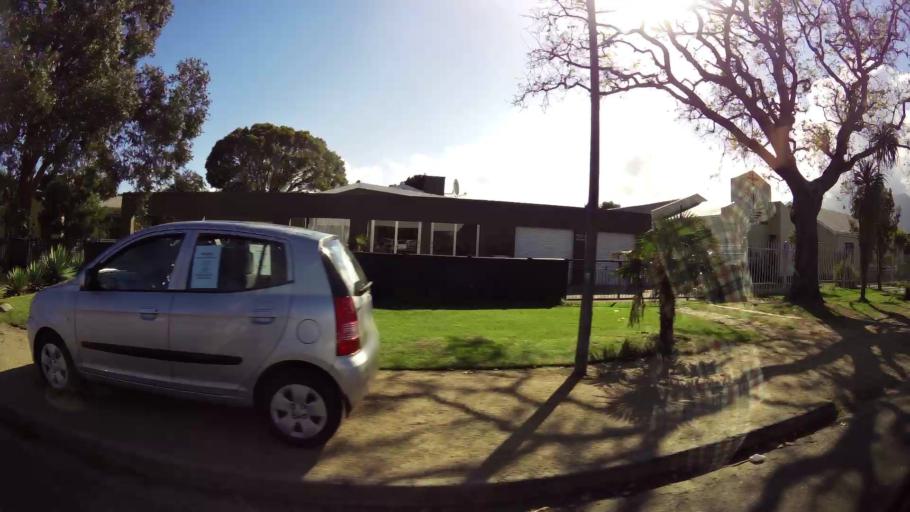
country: ZA
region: Western Cape
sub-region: Eden District Municipality
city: George
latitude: -33.9682
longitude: 22.4537
